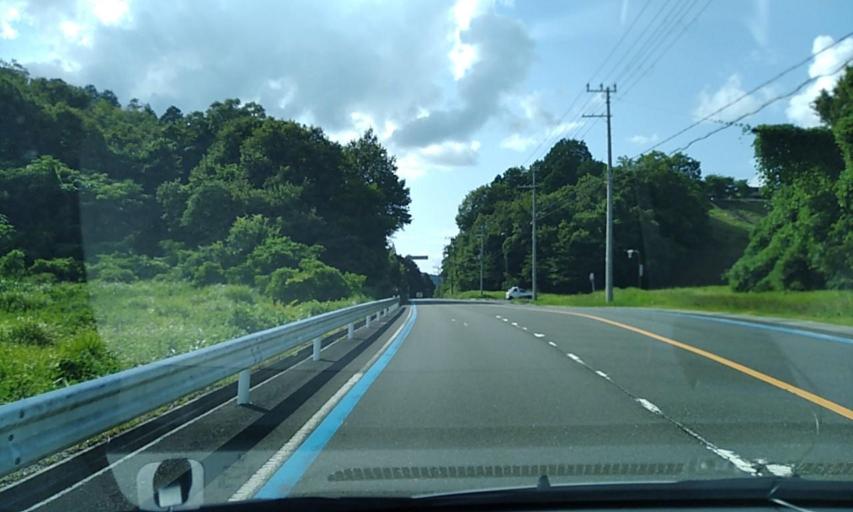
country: JP
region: Kyoto
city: Ayabe
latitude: 35.3155
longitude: 135.2770
